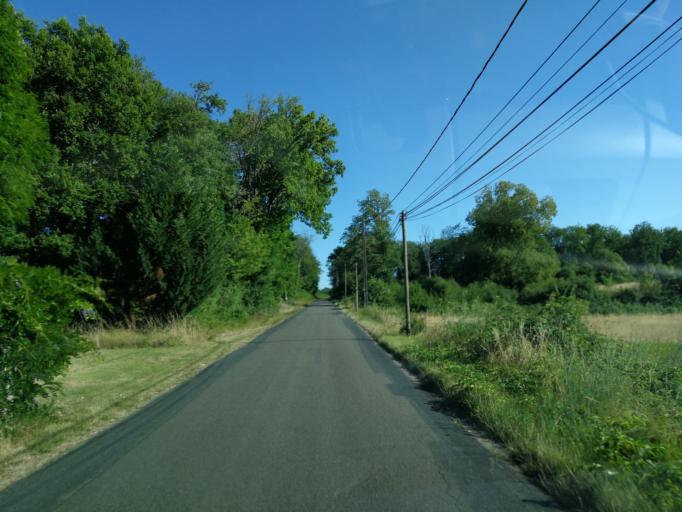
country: FR
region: Midi-Pyrenees
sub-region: Departement du Lot
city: Gourdon
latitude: 44.7738
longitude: 1.3673
